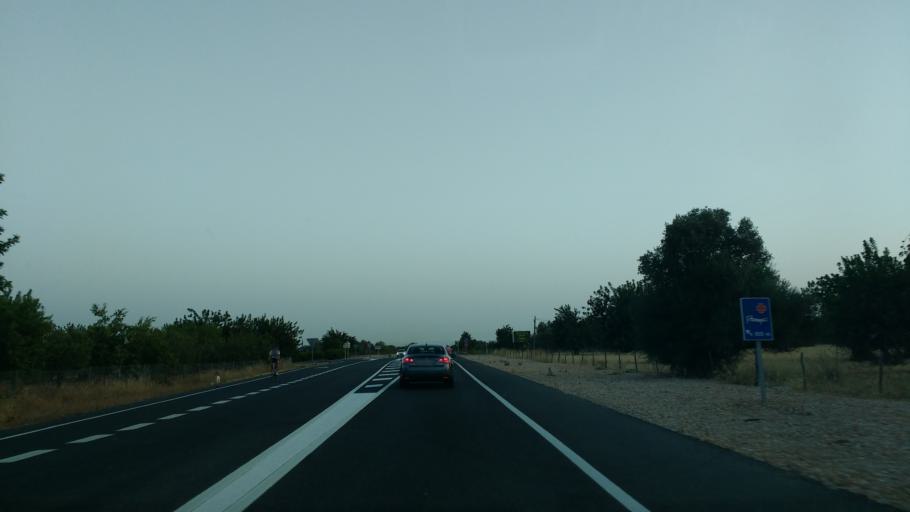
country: ES
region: Balearic Islands
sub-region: Illes Balears
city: Bunyola
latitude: 39.6763
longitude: 2.6796
